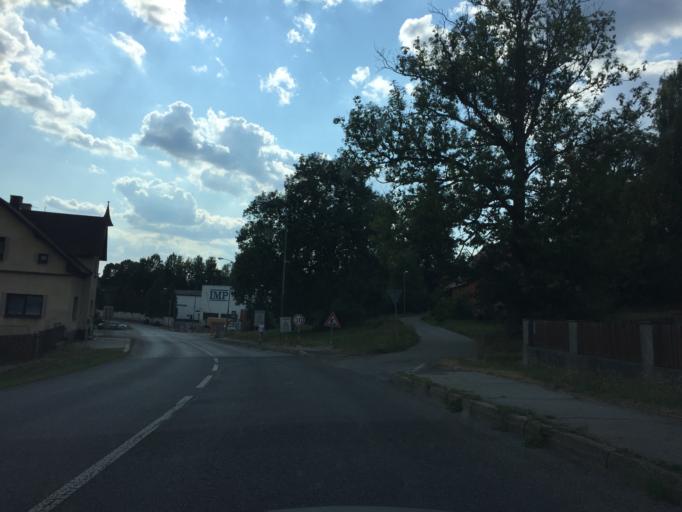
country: CZ
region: Liberecky
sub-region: Okres Jablonec nad Nisou
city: Jablonec nad Nisou
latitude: 50.6996
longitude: 15.1685
